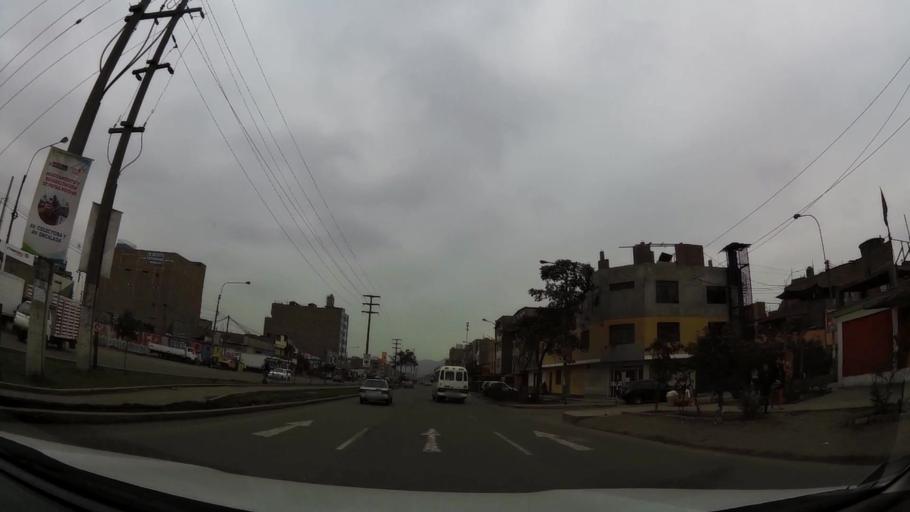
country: PE
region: Lima
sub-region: Lima
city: Vitarte
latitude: -12.0359
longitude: -76.9495
